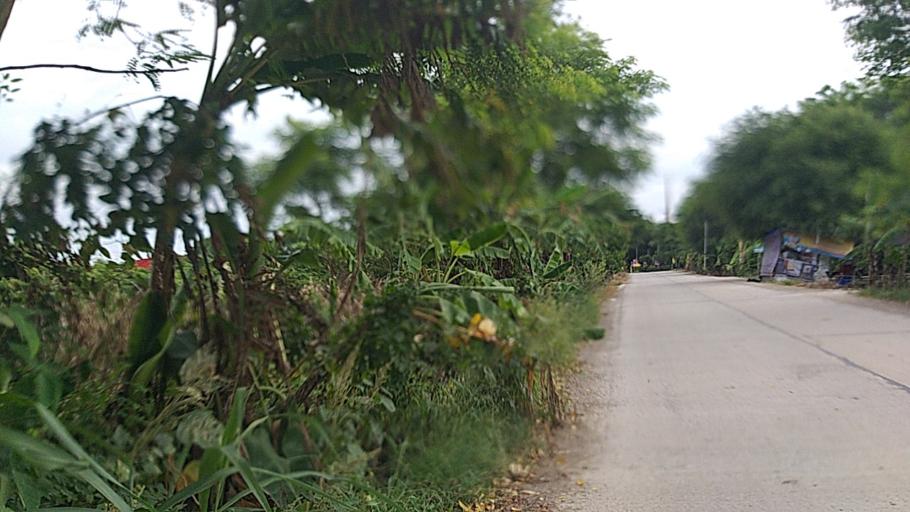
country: TH
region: Pathum Thani
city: Ban Lam Luk Ka
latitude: 14.0355
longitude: 100.8664
